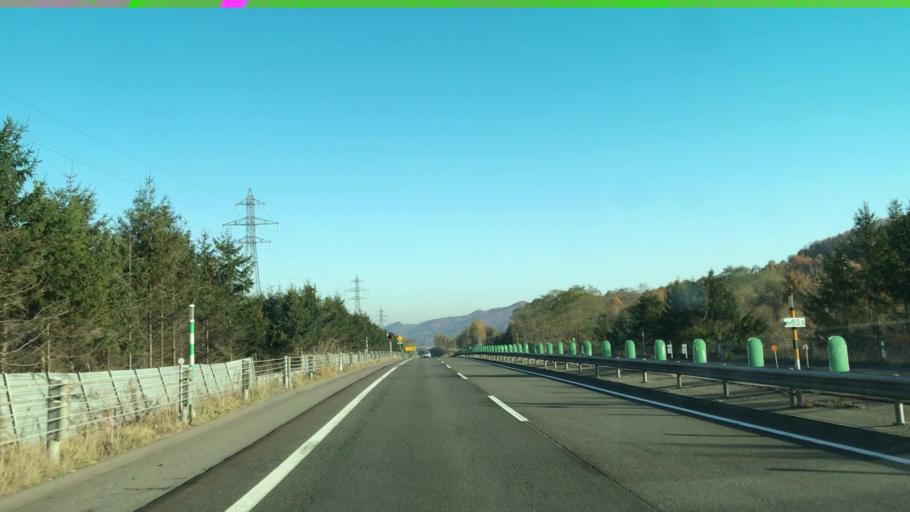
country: JP
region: Hokkaido
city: Sunagawa
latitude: 43.4252
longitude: 141.9121
